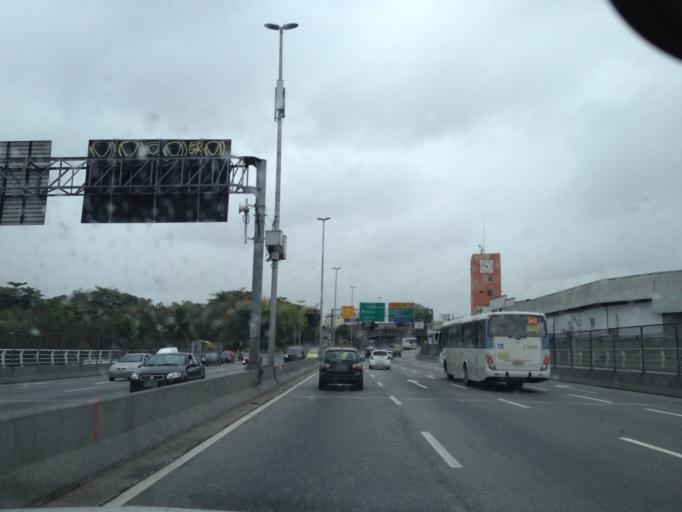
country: BR
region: Rio de Janeiro
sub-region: Rio De Janeiro
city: Rio de Janeiro
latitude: -22.8709
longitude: -43.2460
